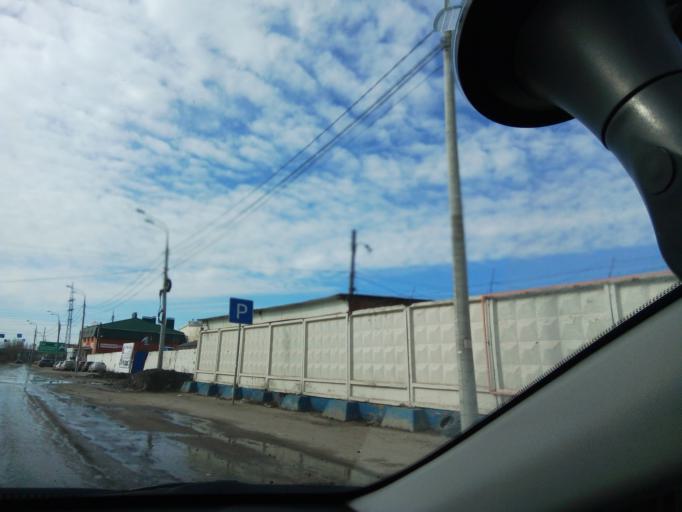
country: RU
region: Chuvashia
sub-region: Cheboksarskiy Rayon
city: Cheboksary
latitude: 56.1063
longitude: 47.2480
